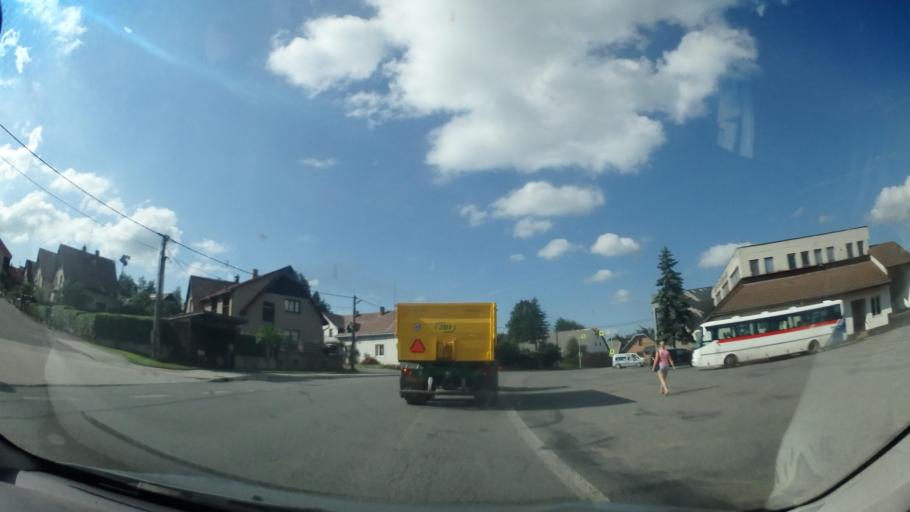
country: CZ
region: Vysocina
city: Heralec
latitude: 49.6904
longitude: 15.9916
